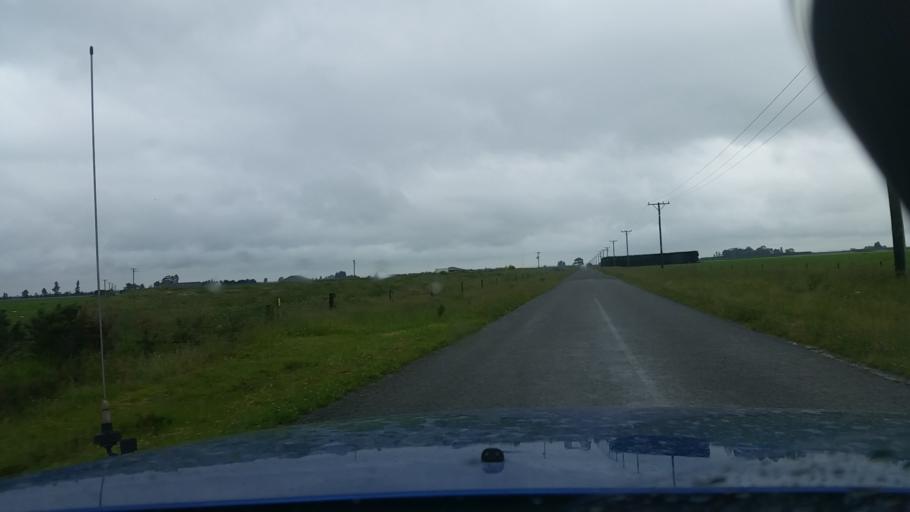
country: NZ
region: Canterbury
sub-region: Ashburton District
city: Tinwald
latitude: -43.8775
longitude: 171.6430
